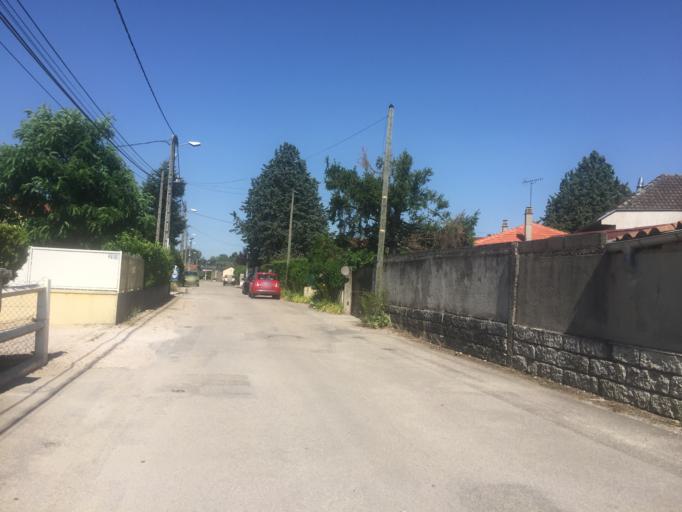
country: FR
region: Rhone-Alpes
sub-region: Departement de l'Ain
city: La Boisse
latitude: 45.8416
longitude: 5.0399
